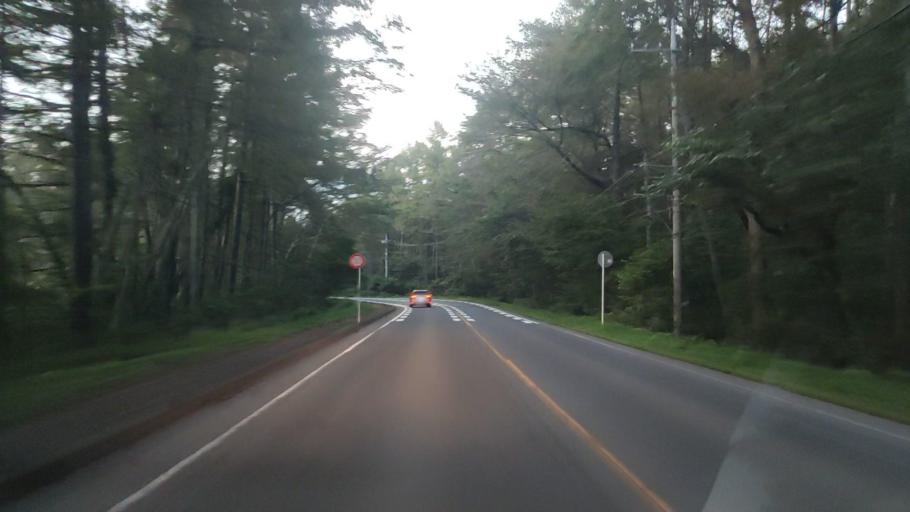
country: JP
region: Gunma
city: Nakanojomachi
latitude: 36.5241
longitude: 138.5996
